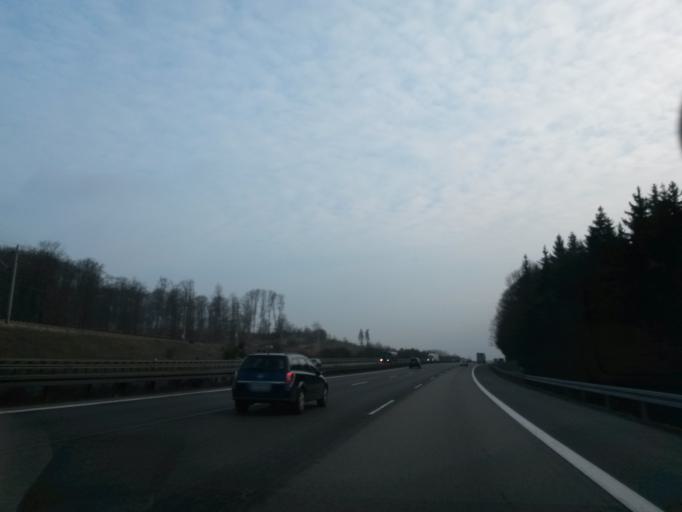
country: DE
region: Bavaria
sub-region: Upper Bavaria
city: Denkendorf
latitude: 48.9037
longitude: 11.4700
